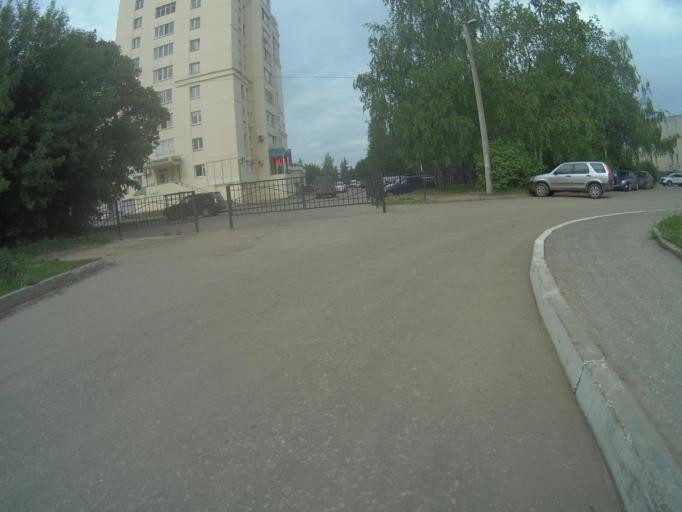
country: RU
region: Vladimir
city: Kommunar
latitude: 56.1653
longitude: 40.4643
